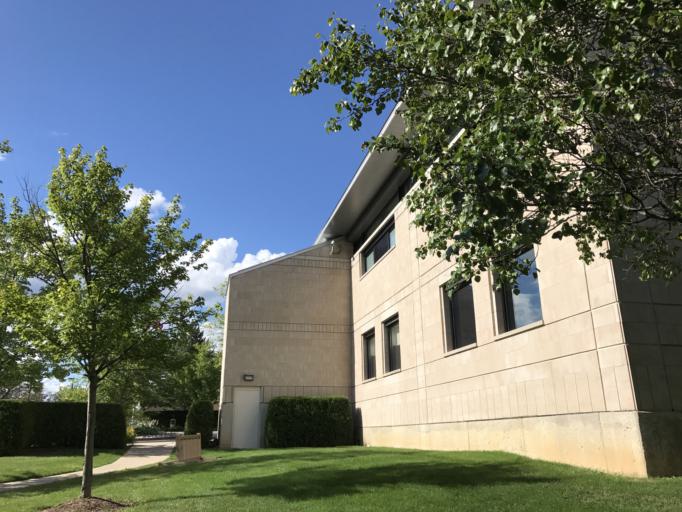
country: US
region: Michigan
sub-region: Oakland County
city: Farmington Hills
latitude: 42.4976
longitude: -83.3713
